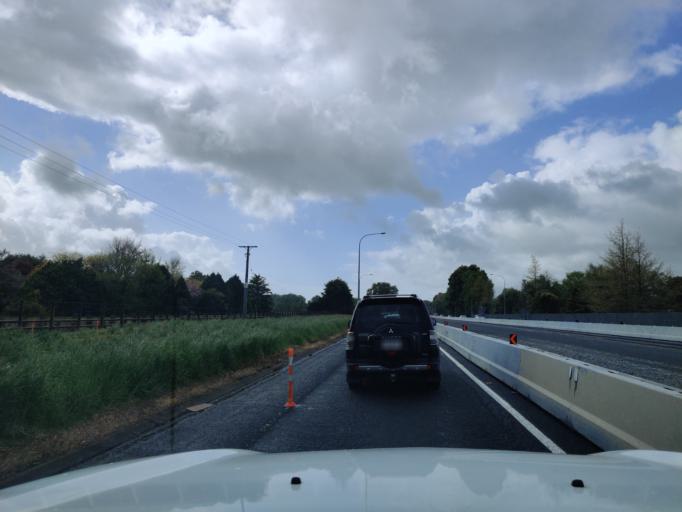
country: NZ
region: Waikato
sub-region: Hamilton City
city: Hamilton
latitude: -37.8252
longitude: 175.3537
